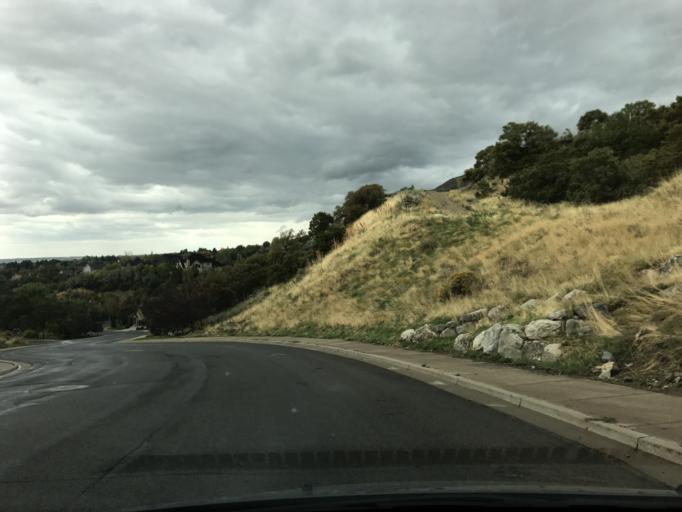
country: US
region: Utah
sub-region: Davis County
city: Fruit Heights
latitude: 41.0158
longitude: -111.8988
